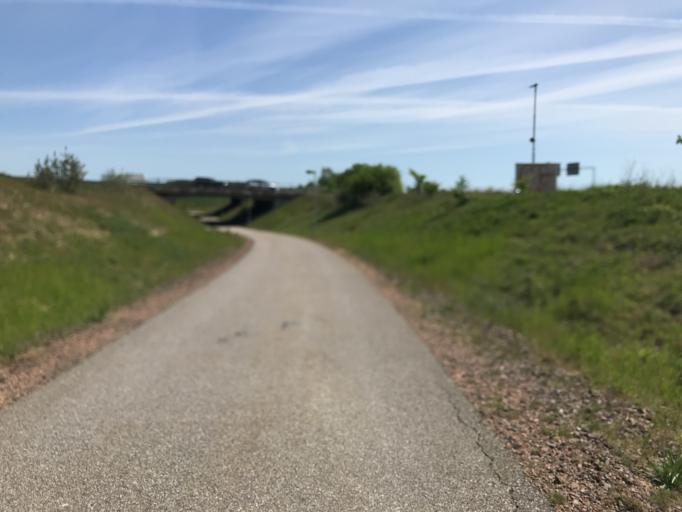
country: SE
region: Skane
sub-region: Malmo
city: Oxie
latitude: 55.5574
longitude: 13.0720
